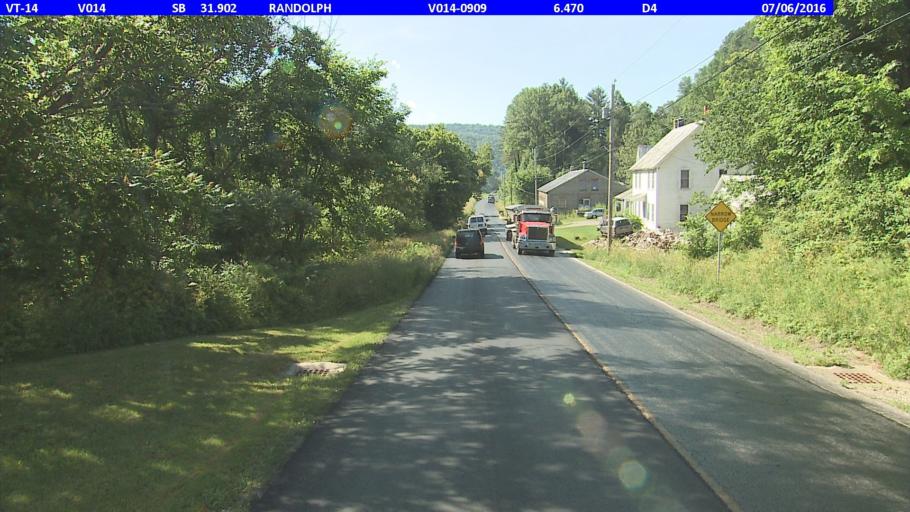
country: US
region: Vermont
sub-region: Orange County
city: Chelsea
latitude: 43.9615
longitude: -72.5521
